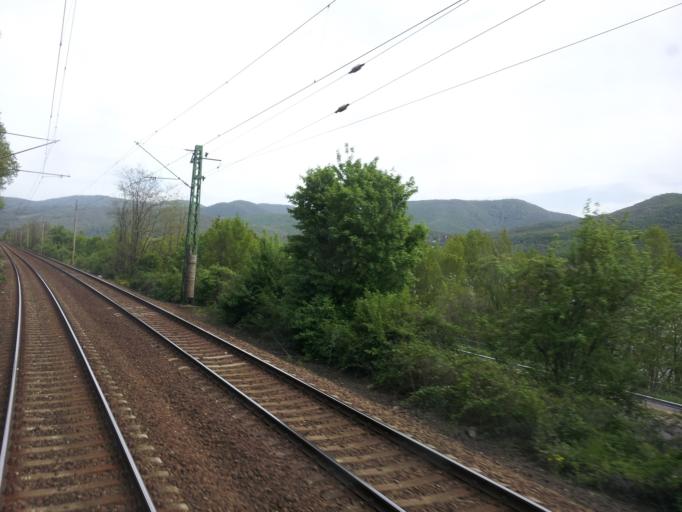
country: HU
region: Pest
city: Nagymaros
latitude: 47.7682
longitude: 18.9286
